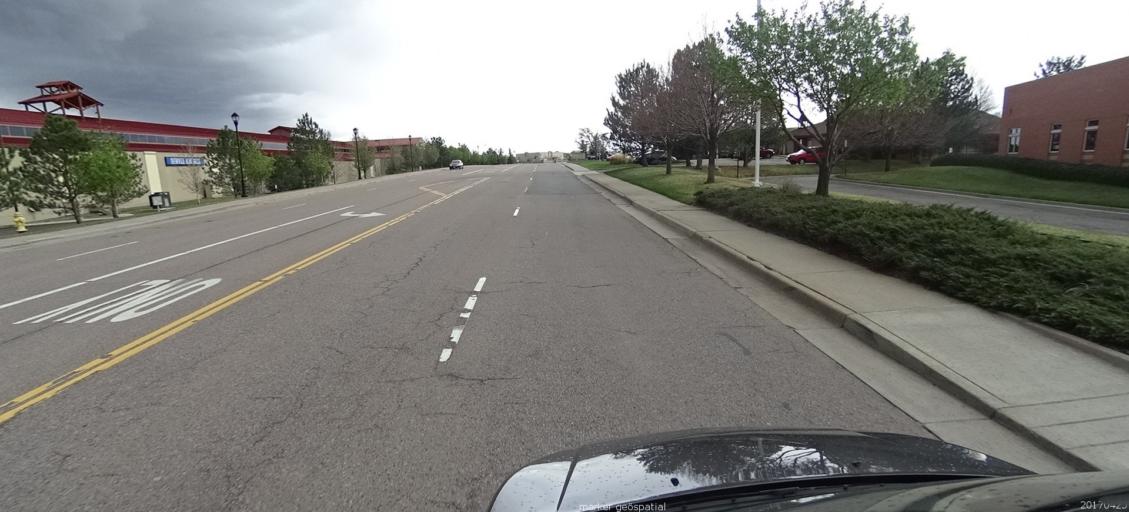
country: US
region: Colorado
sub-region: Douglas County
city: Acres Green
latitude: 39.5629
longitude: -104.8957
